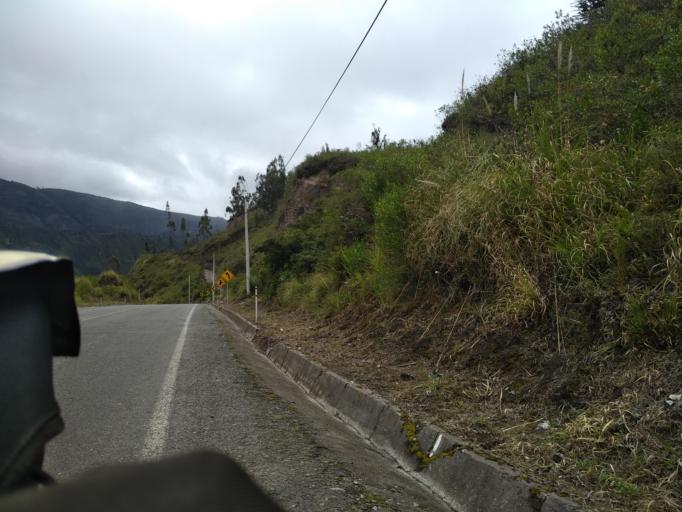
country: EC
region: Chimborazo
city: Guano
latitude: -1.5516
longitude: -78.5352
